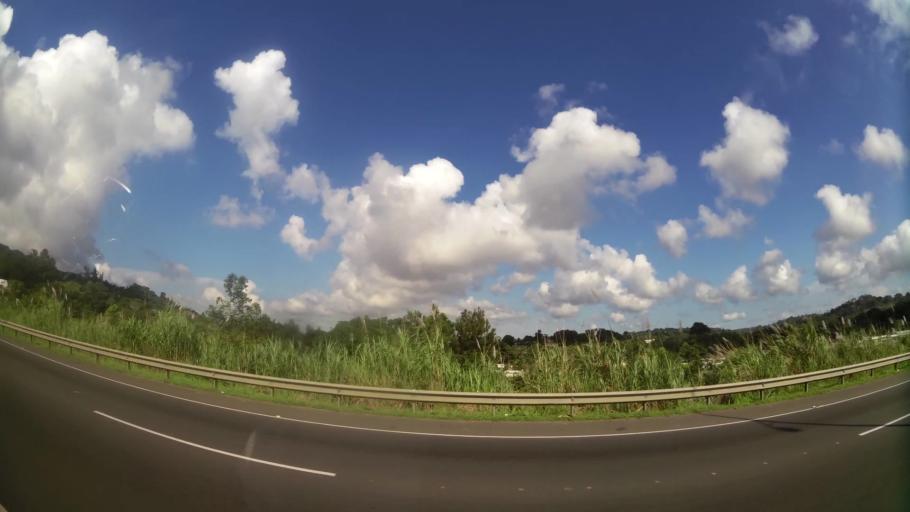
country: PA
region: Panama
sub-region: Distrito Arraijan
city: Arraijan
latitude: 8.9462
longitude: -79.6668
